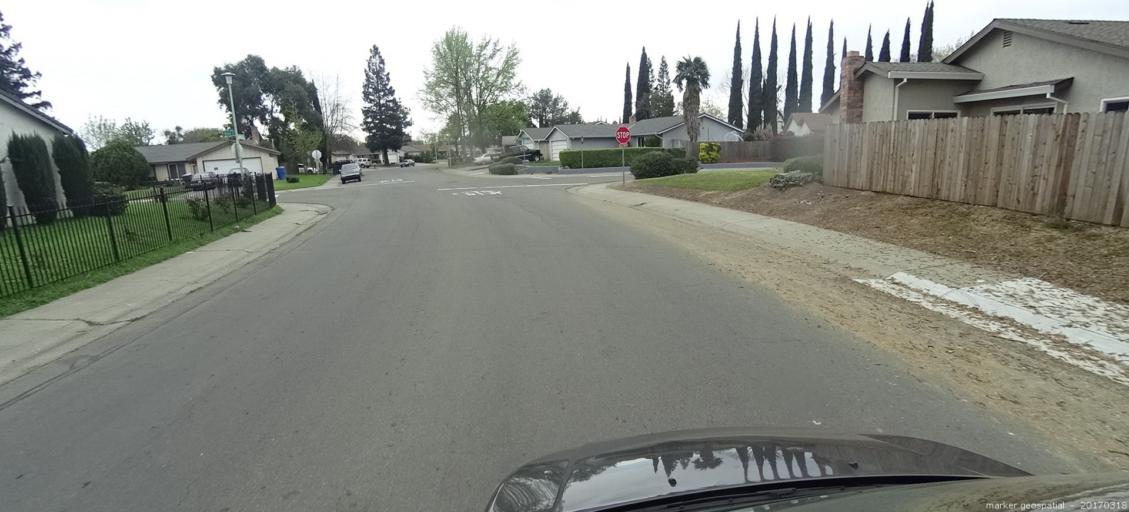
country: US
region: California
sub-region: Sacramento County
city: Florin
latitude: 38.4776
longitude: -121.4323
